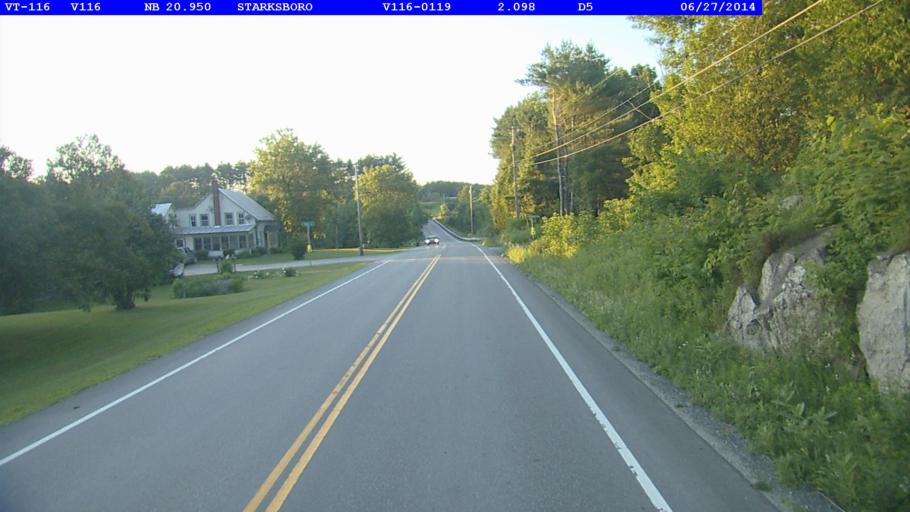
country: US
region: Vermont
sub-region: Addison County
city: Bristol
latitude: 44.2149
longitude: -73.0551
